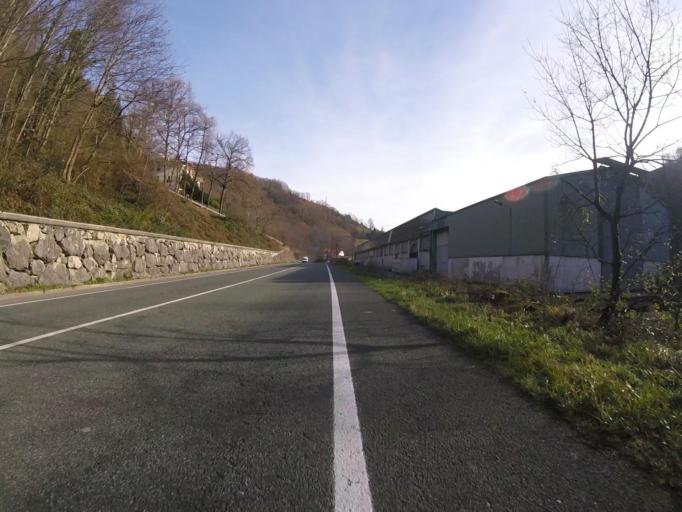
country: ES
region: Navarre
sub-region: Provincia de Navarra
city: Leitza
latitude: 43.0902
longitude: -1.9308
